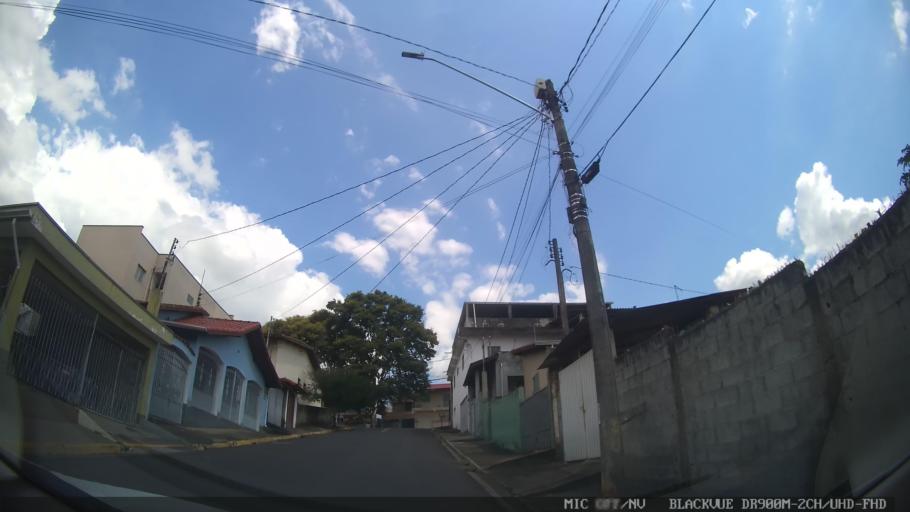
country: BR
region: Minas Gerais
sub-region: Extrema
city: Extrema
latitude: -22.8585
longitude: -46.3274
